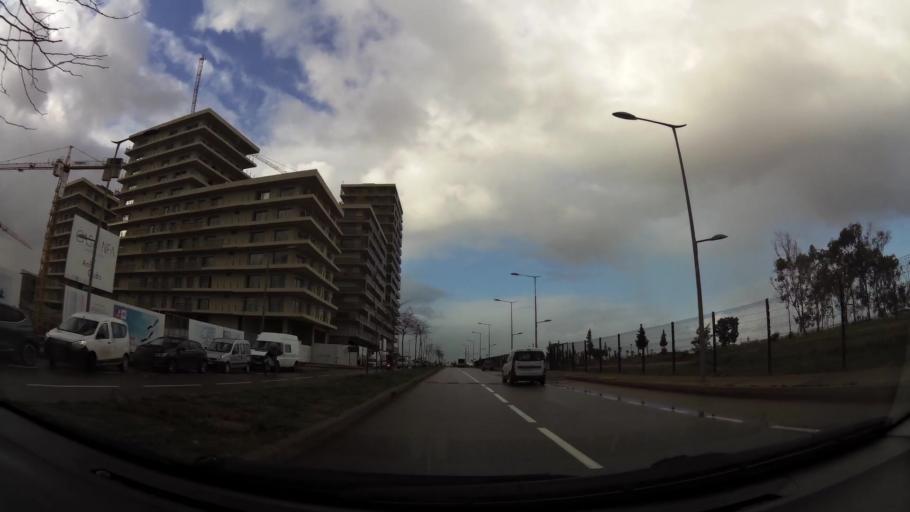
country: MA
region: Grand Casablanca
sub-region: Casablanca
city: Casablanca
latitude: 33.5609
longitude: -7.6560
